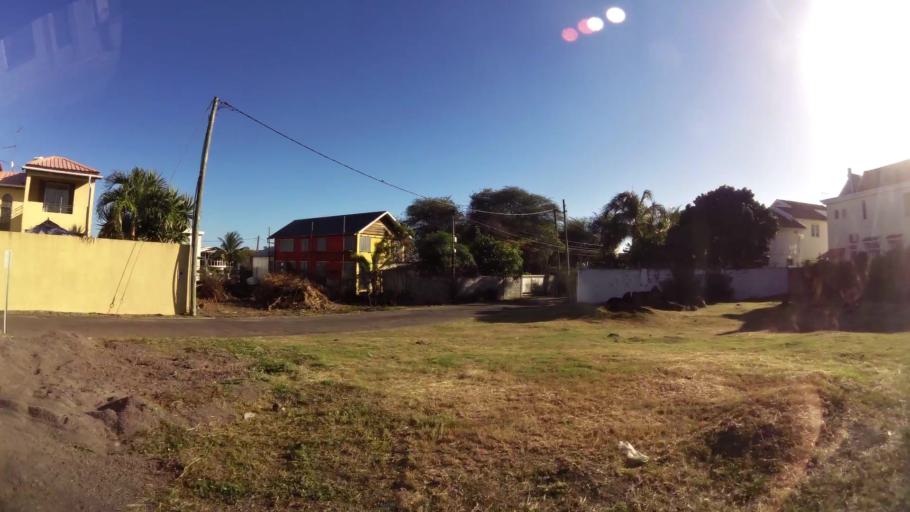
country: MU
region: Black River
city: Tamarin
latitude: -20.3367
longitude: 57.3730
